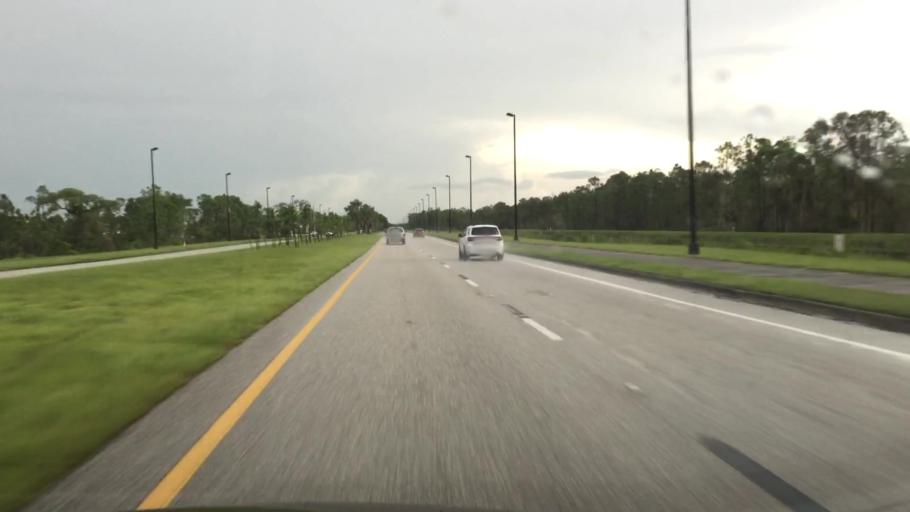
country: US
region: Florida
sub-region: Lee County
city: Three Oaks
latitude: 26.5258
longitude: -81.7852
